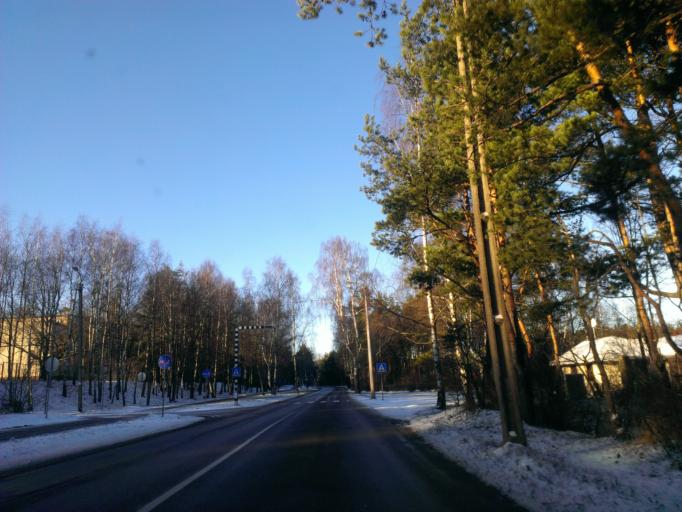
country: LV
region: Riga
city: Bolderaja
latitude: 57.0352
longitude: 24.1140
